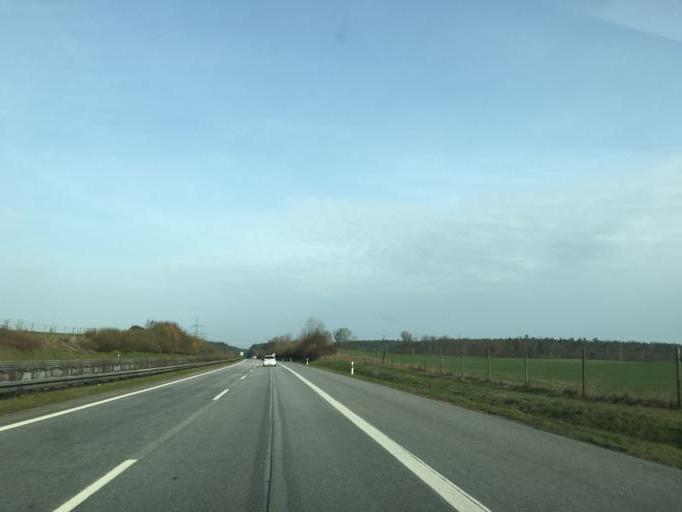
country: DE
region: Mecklenburg-Vorpommern
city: Malchow
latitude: 53.4364
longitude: 12.4131
